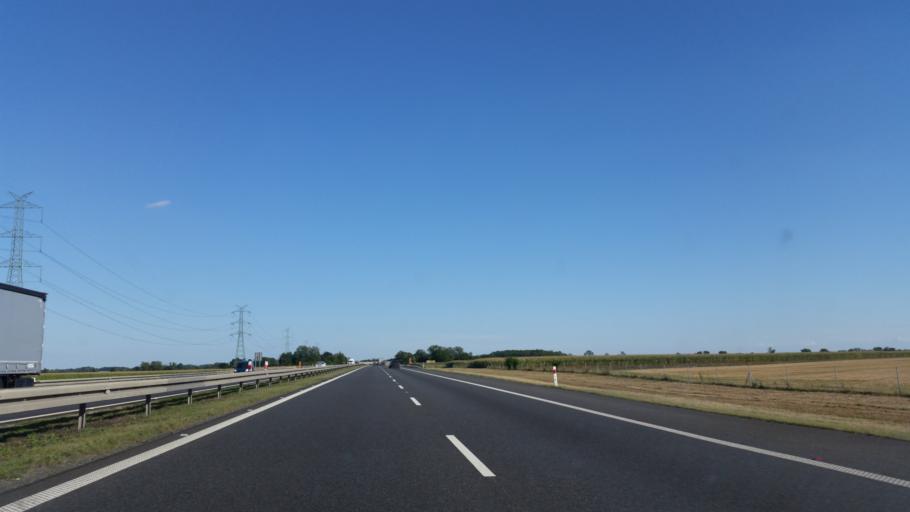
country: PL
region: Lower Silesian Voivodeship
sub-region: Powiat olawski
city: Wierzbno
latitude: 50.9254
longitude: 17.1271
